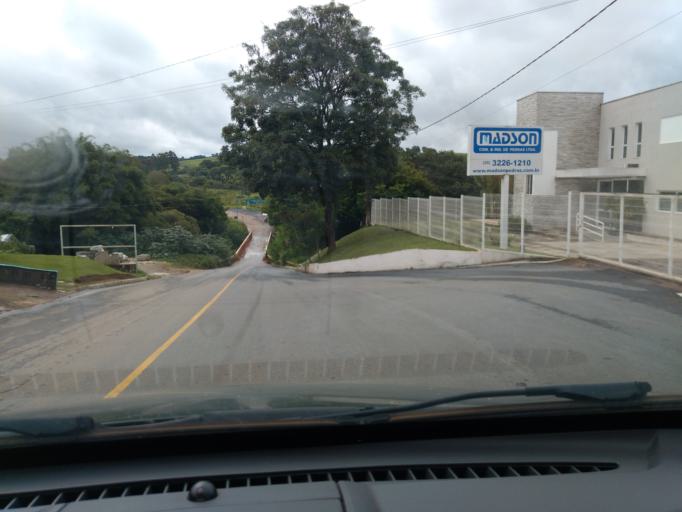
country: BR
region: Minas Gerais
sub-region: Lavras
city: Lavras
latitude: -21.5064
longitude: -44.9149
